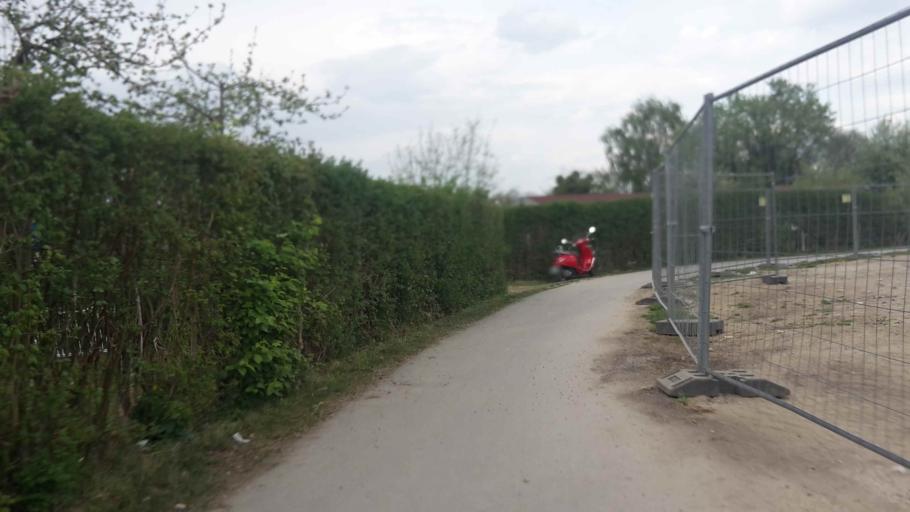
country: DE
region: Bavaria
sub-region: Upper Bavaria
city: Karlsfeld
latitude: 48.1846
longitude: 11.4922
